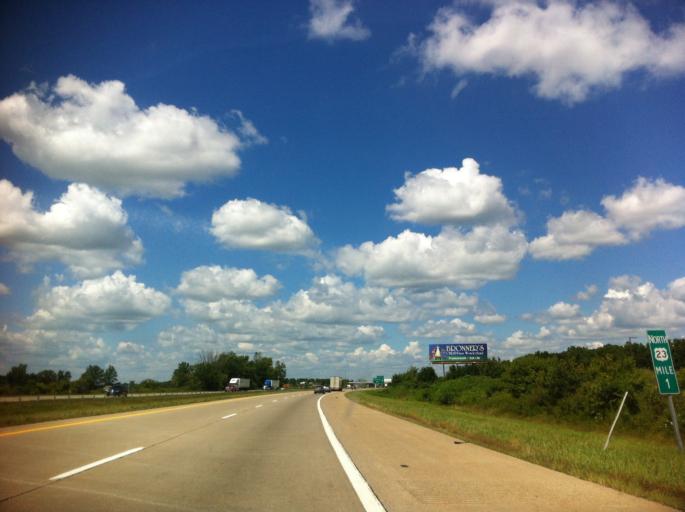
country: US
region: Ohio
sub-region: Lucas County
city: Sylvania
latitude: 41.7400
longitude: -83.6934
